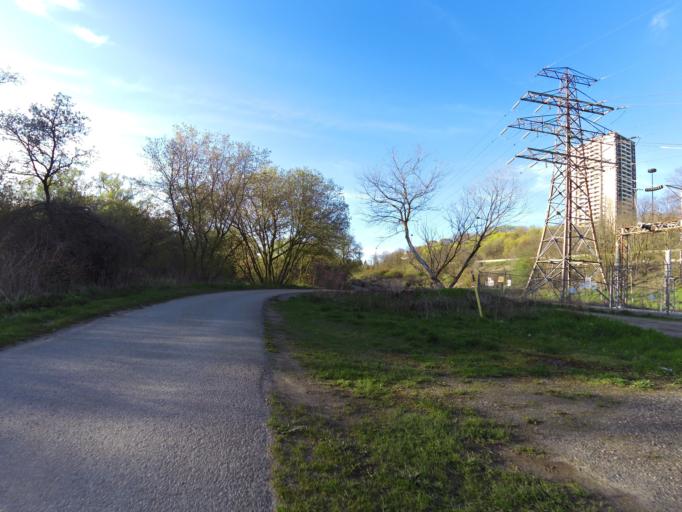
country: CA
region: Ontario
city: Toronto
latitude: 43.6774
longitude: -79.3635
